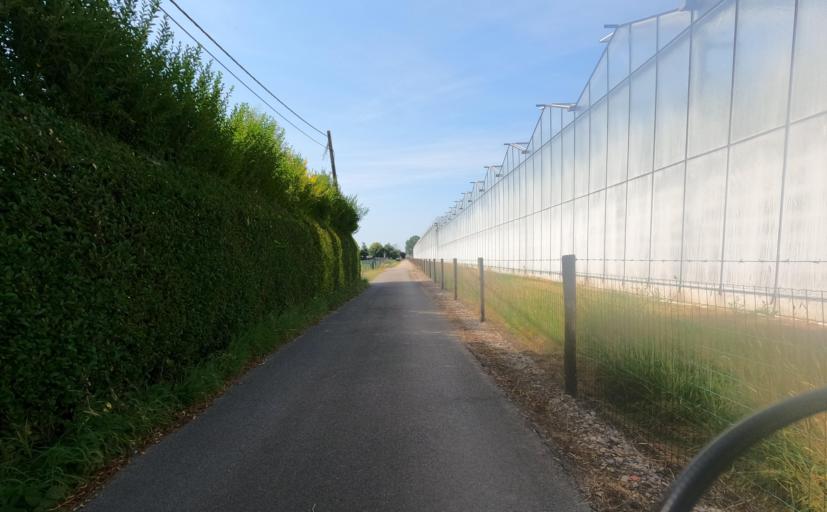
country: BE
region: Flanders
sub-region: Provincie Antwerpen
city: Bonheiden
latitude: 51.0495
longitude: 4.5833
